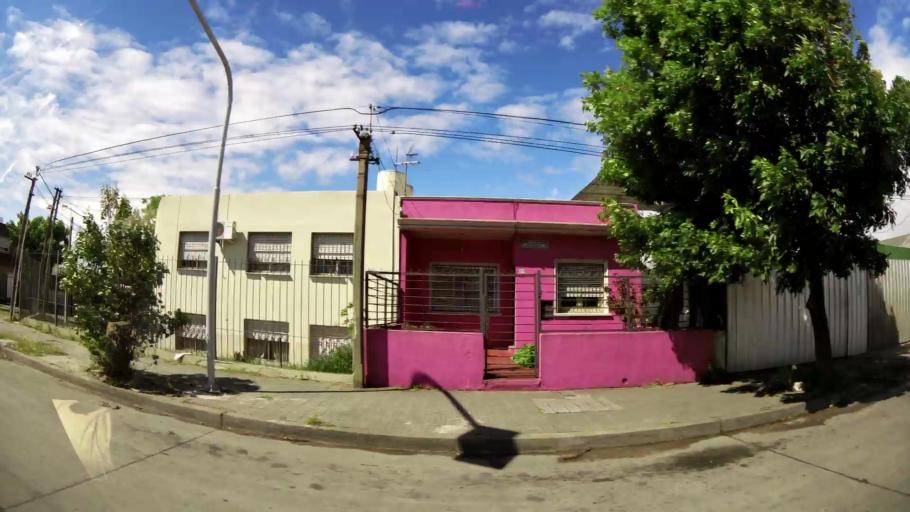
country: UY
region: Montevideo
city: Montevideo
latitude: -34.8518
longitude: -56.1833
